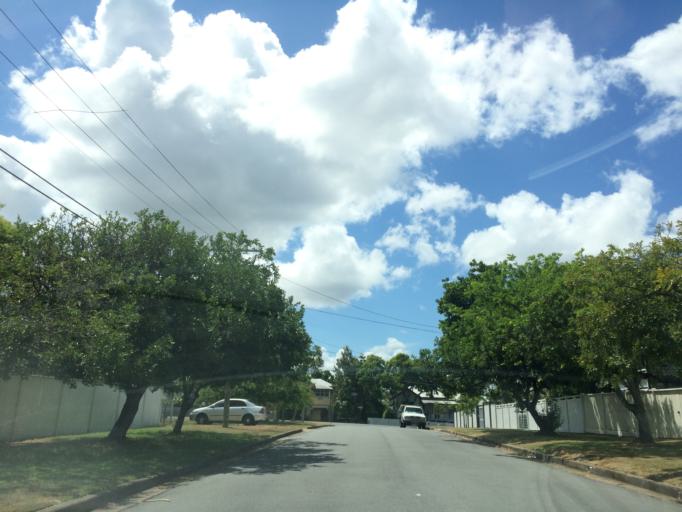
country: AU
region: Queensland
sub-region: Brisbane
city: Seven Hills
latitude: -27.4873
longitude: 153.0603
